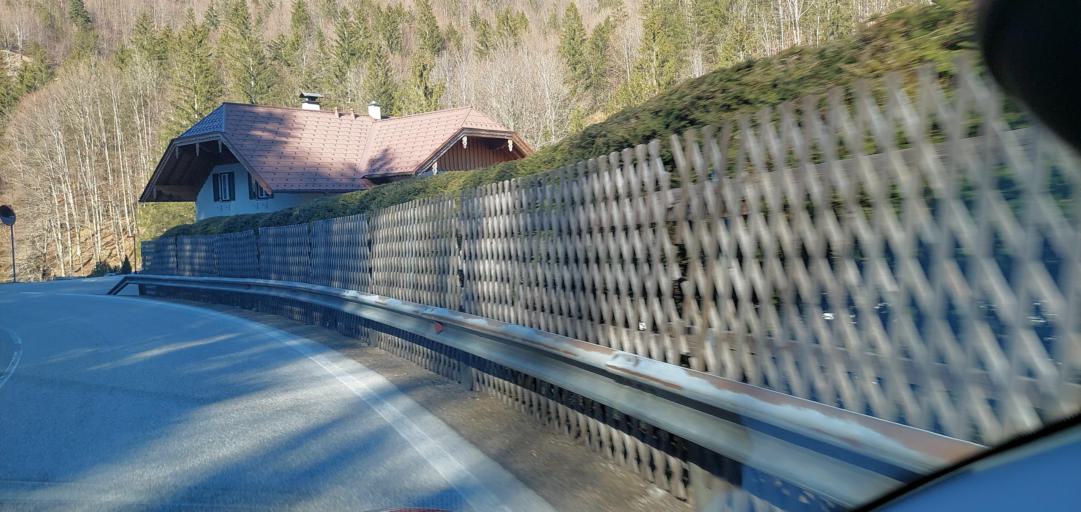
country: AT
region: Upper Austria
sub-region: Politischer Bezirk Gmunden
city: Bad Ischl
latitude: 47.7460
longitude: 13.6641
